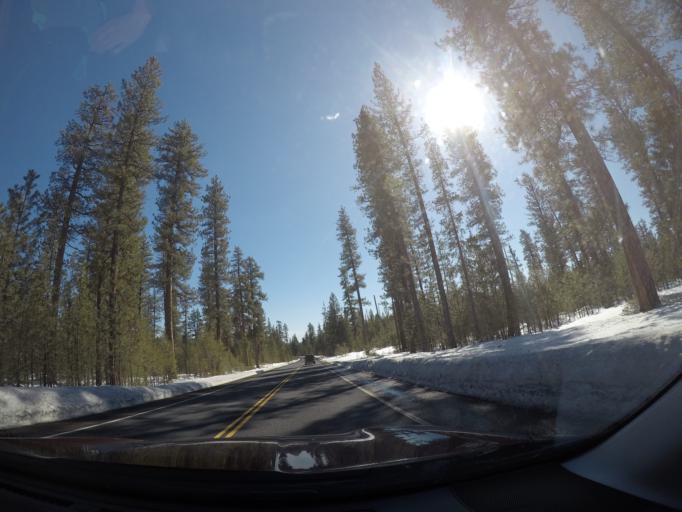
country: US
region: Oregon
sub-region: Deschutes County
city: Three Rivers
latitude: 43.8946
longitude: -121.5901
